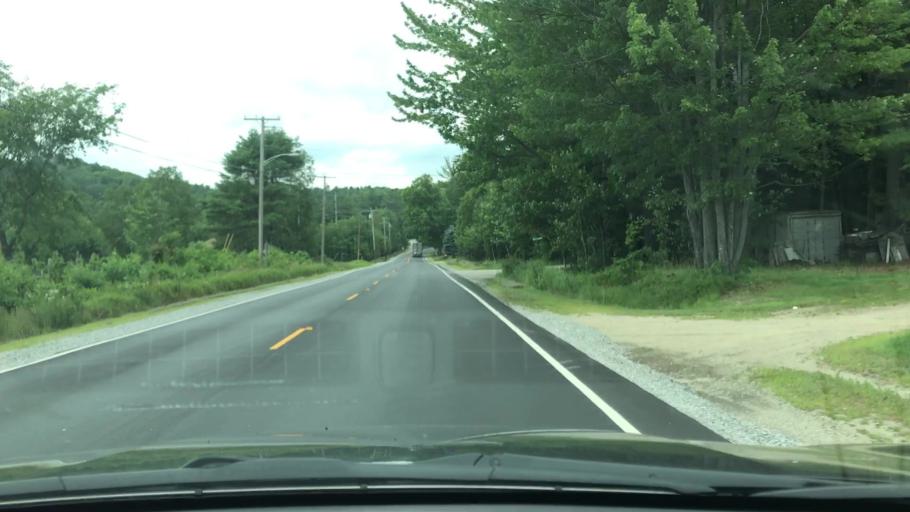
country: US
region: Maine
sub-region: Oxford County
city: West Paris
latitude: 44.3862
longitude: -70.6558
